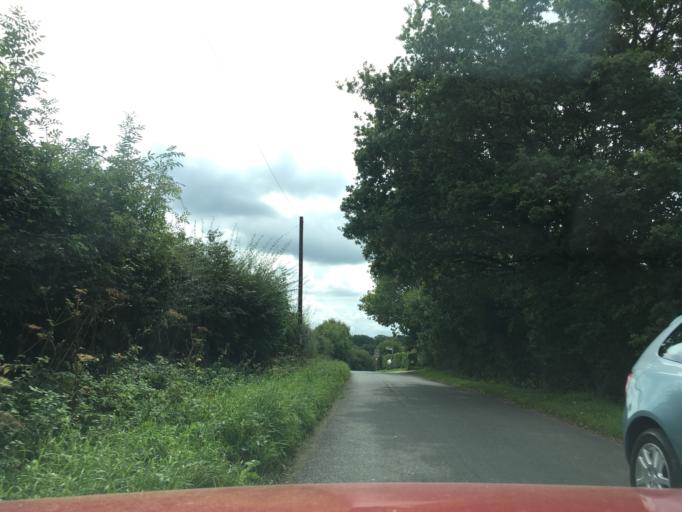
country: GB
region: England
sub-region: South Gloucestershire
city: Charfield
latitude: 51.6480
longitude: -2.4224
